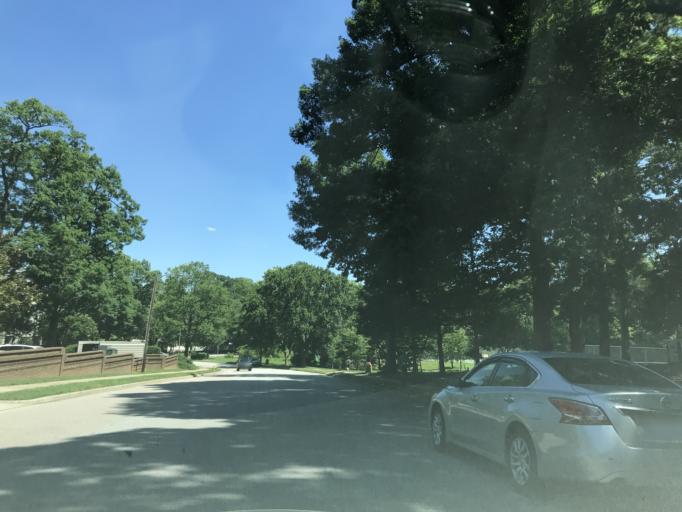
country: US
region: North Carolina
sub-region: Wake County
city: West Raleigh
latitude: 35.7938
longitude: -78.6485
